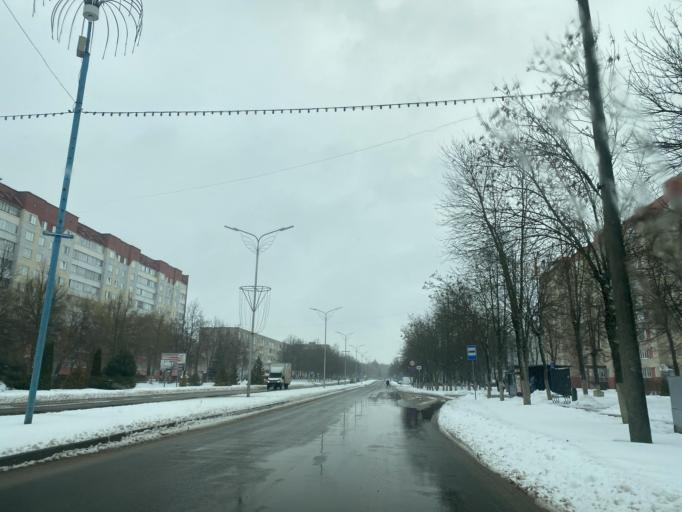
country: BY
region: Minsk
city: Horad Zhodzina
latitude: 54.0950
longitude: 28.3052
